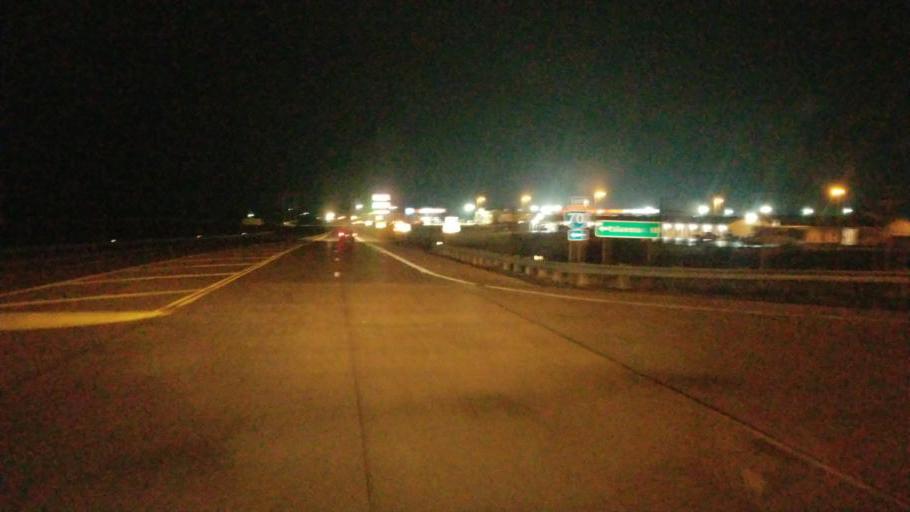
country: US
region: Ohio
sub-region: Preble County
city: Lewisburg
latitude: 39.8342
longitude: -84.6294
